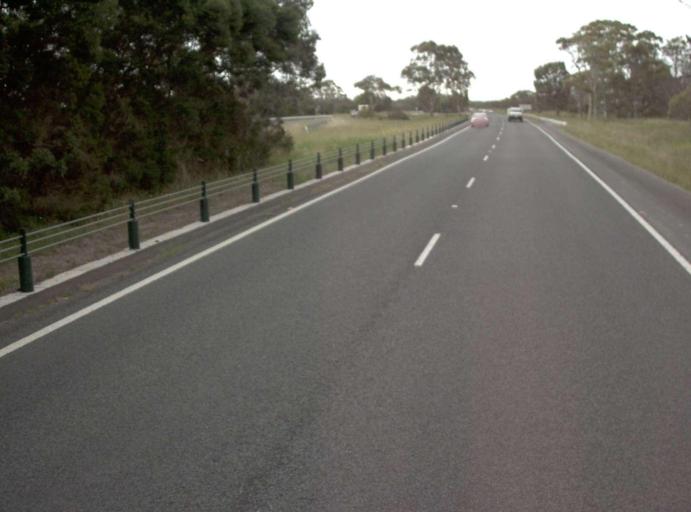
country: AU
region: Victoria
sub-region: Casey
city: Blind Bight
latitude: -38.1849
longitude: 145.3434
